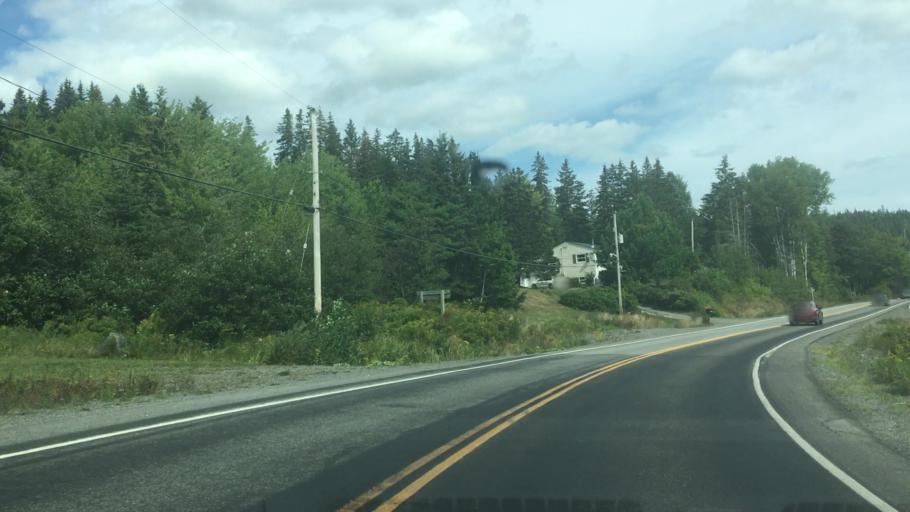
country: CA
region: Nova Scotia
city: Sydney Mines
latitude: 46.2644
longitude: -60.6241
